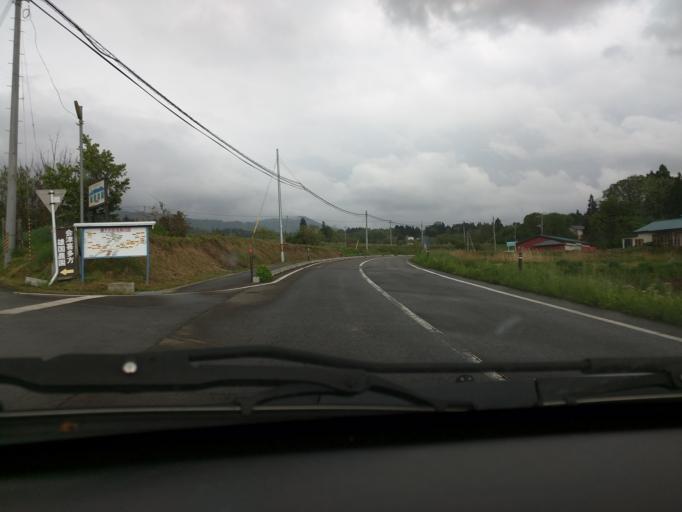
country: JP
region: Fukushima
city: Kitakata
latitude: 37.6370
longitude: 139.9334
